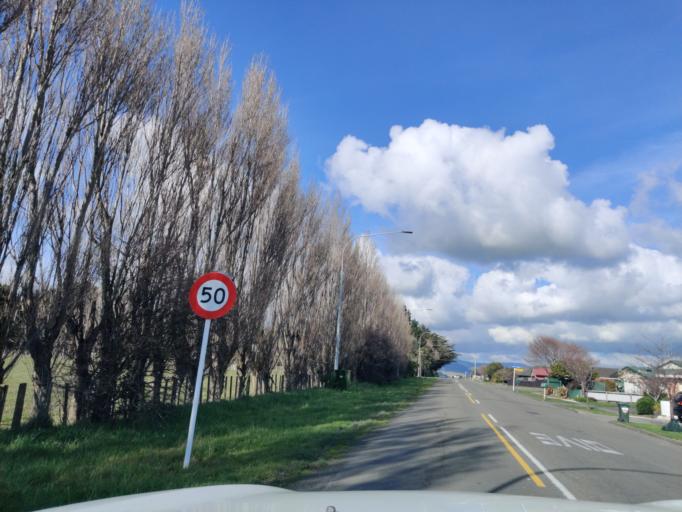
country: NZ
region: Manawatu-Wanganui
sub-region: Palmerston North City
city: Palmerston North
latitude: -40.3187
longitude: 175.6569
